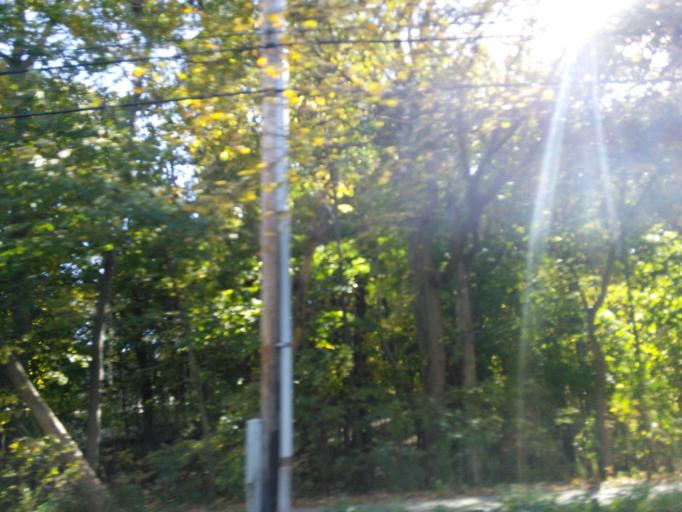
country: US
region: Michigan
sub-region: Washtenaw County
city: Ann Arbor
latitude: 42.2760
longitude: -83.7679
